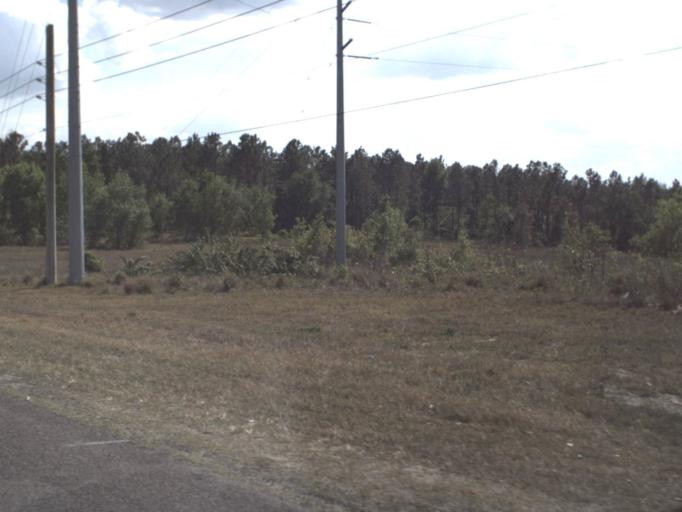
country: US
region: Florida
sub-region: Lake County
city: Minneola
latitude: 28.5956
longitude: -81.7535
